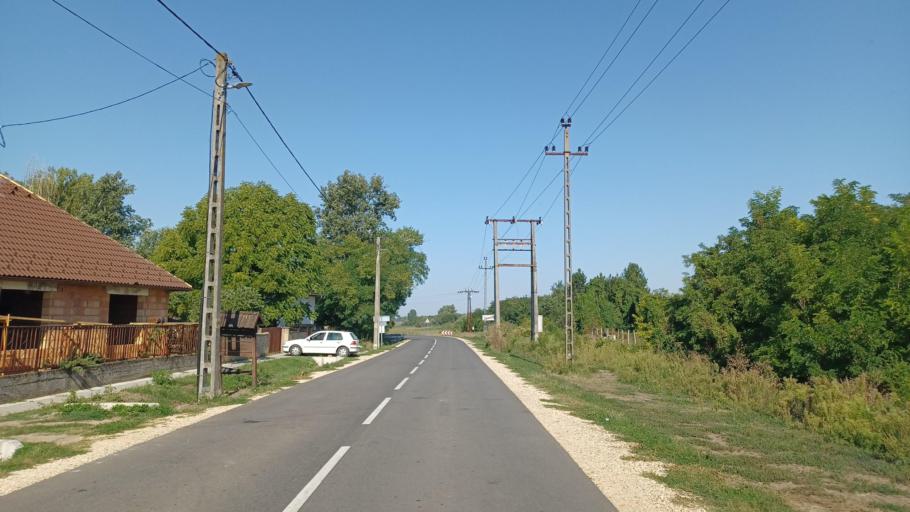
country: HU
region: Tolna
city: Nemetker
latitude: 46.7306
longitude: 18.7474
